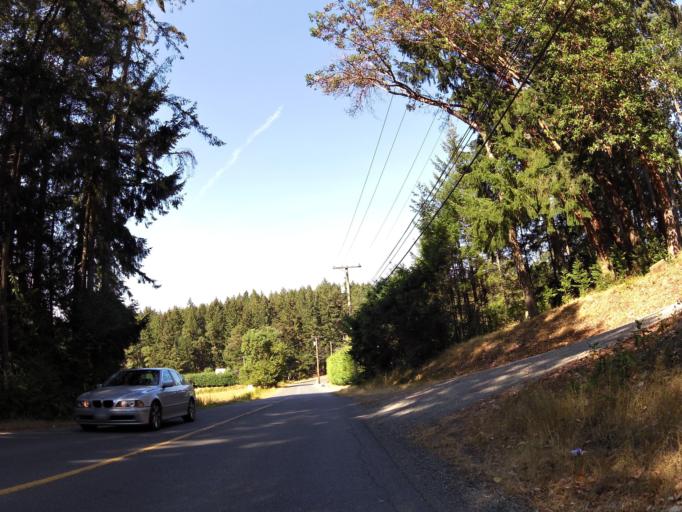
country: CA
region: British Columbia
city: North Saanich
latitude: 48.6700
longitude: -123.5535
